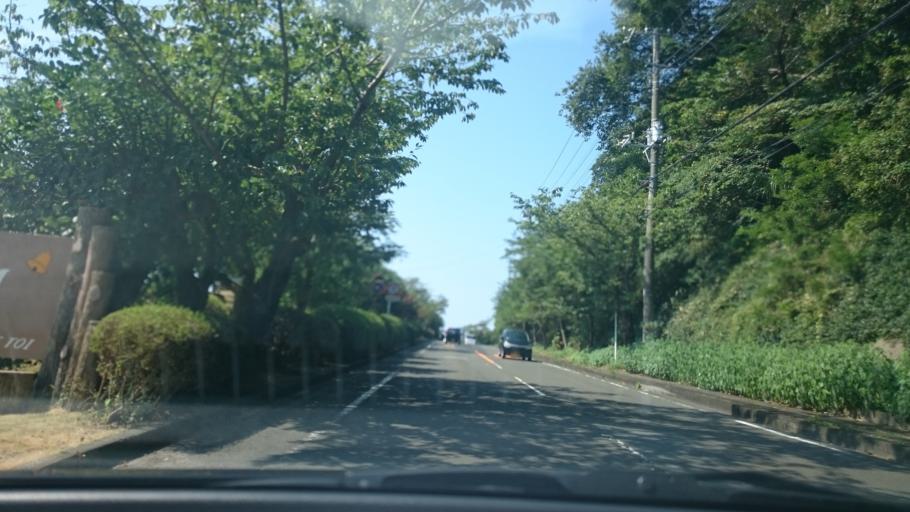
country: JP
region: Shizuoka
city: Heda
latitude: 34.8671
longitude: 138.7620
